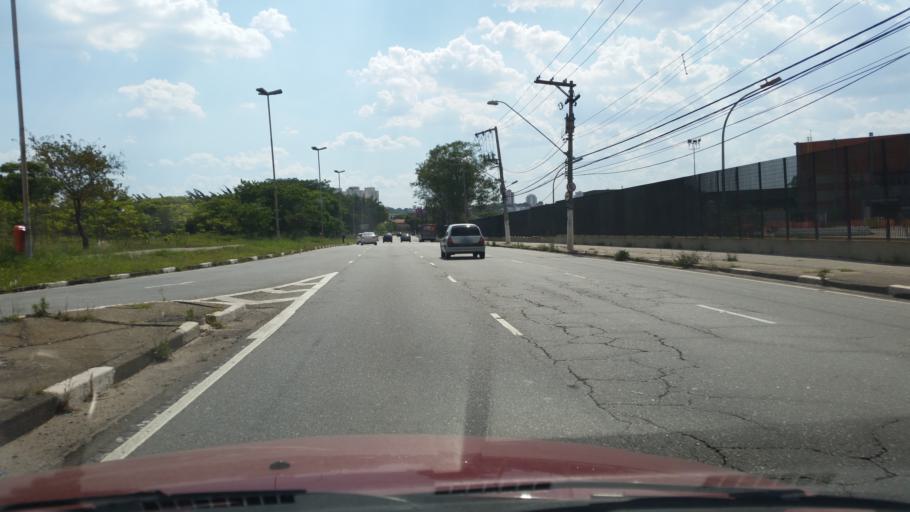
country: BR
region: Sao Paulo
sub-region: Sao Bernardo Do Campo
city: Sao Bernardo do Campo
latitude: -23.6669
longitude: -46.5768
